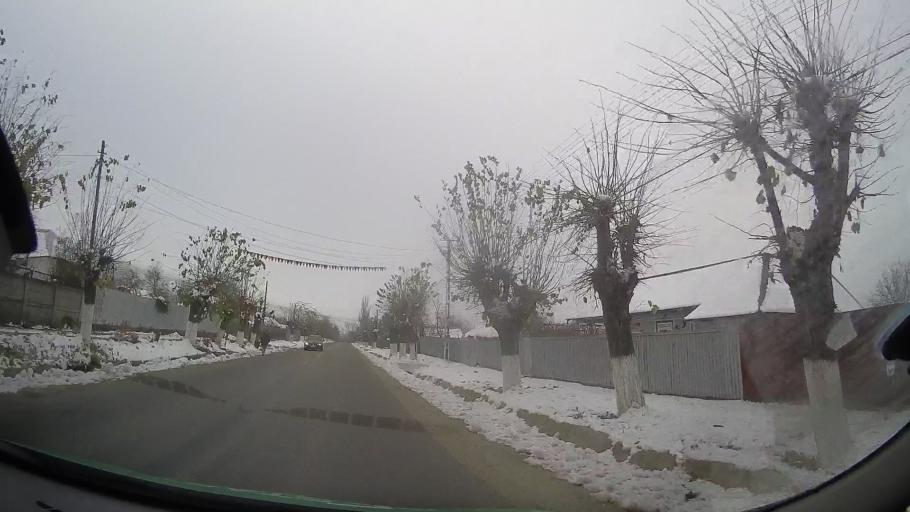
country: RO
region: Bacau
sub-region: Comuna Glavanesti
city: Frumuselu
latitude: 46.2994
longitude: 27.2982
